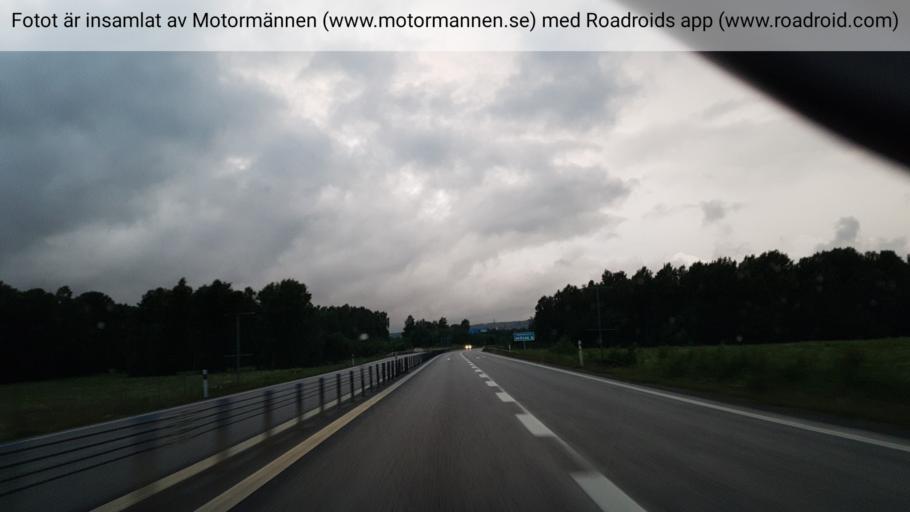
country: SE
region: Vaestra Goetaland
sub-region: Skovde Kommun
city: Skultorp
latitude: 58.3628
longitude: 13.8616
